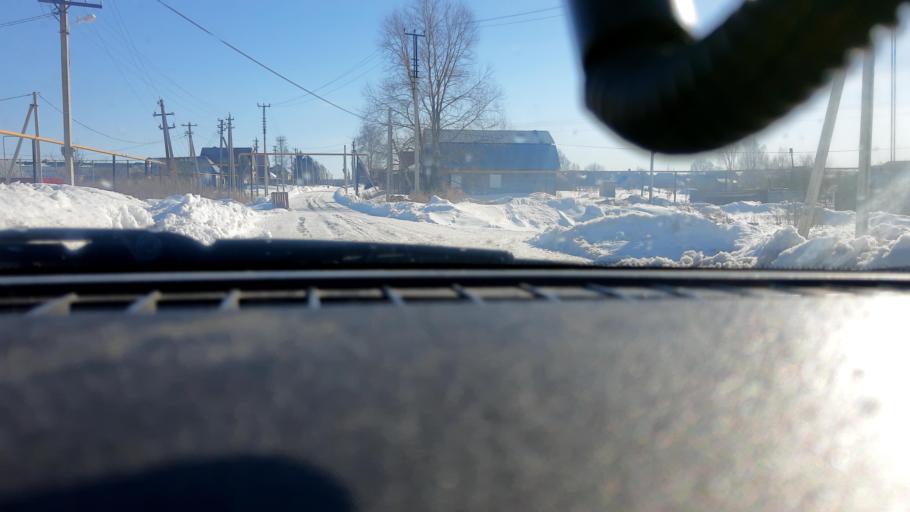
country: RU
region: Bashkortostan
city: Kabakovo
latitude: 54.7432
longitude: 56.1932
